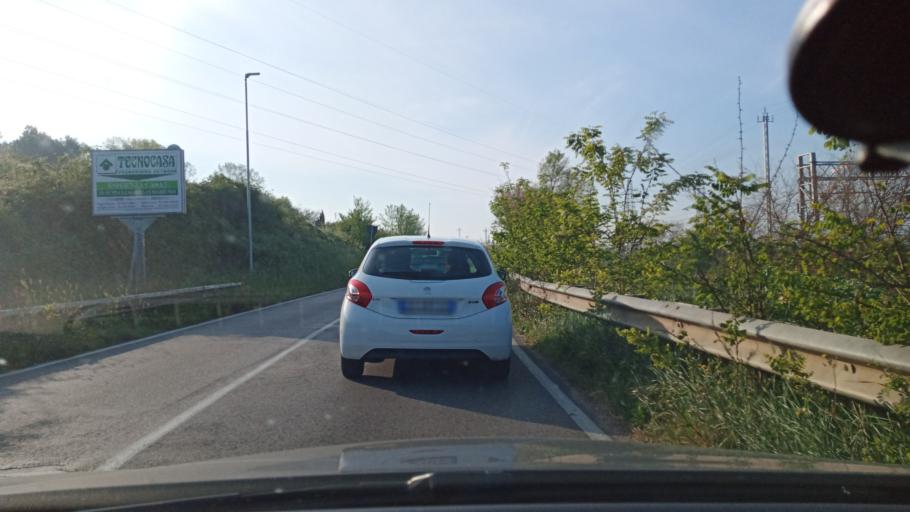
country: IT
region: Latium
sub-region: Citta metropolitana di Roma Capitale
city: Fiano Romano
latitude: 42.1659
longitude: 12.6423
